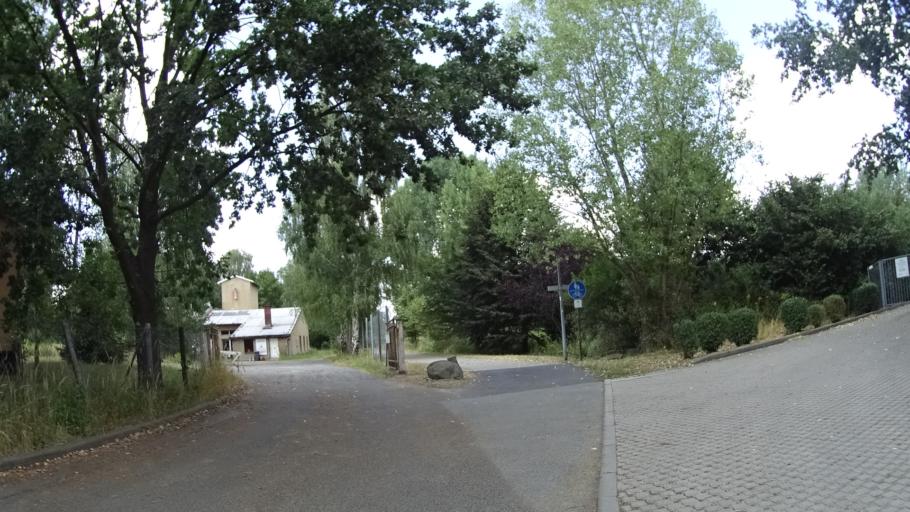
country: DE
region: Saxony
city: Ostritz
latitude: 51.0194
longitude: 14.9321
